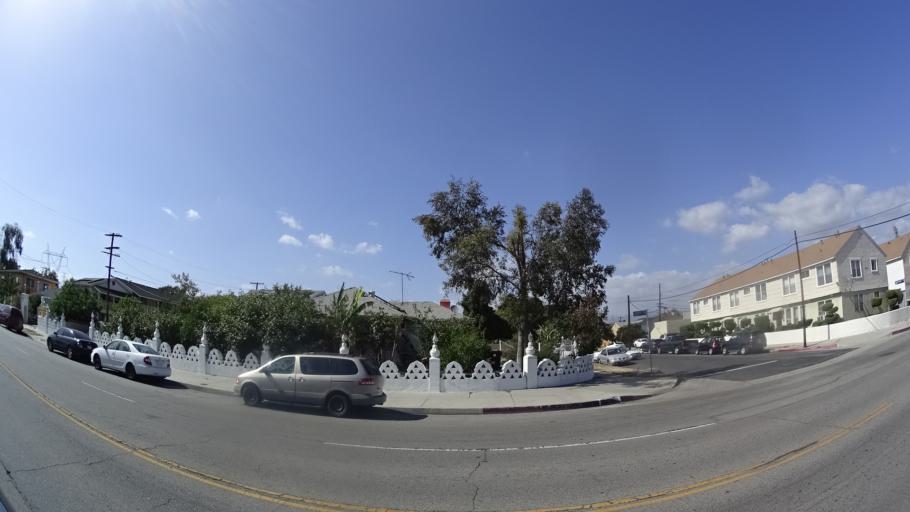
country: US
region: California
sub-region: Los Angeles County
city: North Hollywood
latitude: 34.1794
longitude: -118.3641
